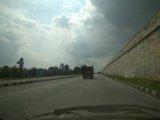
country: IN
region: Karnataka
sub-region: Kolar
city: Malur
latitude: 13.1313
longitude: 77.9848
